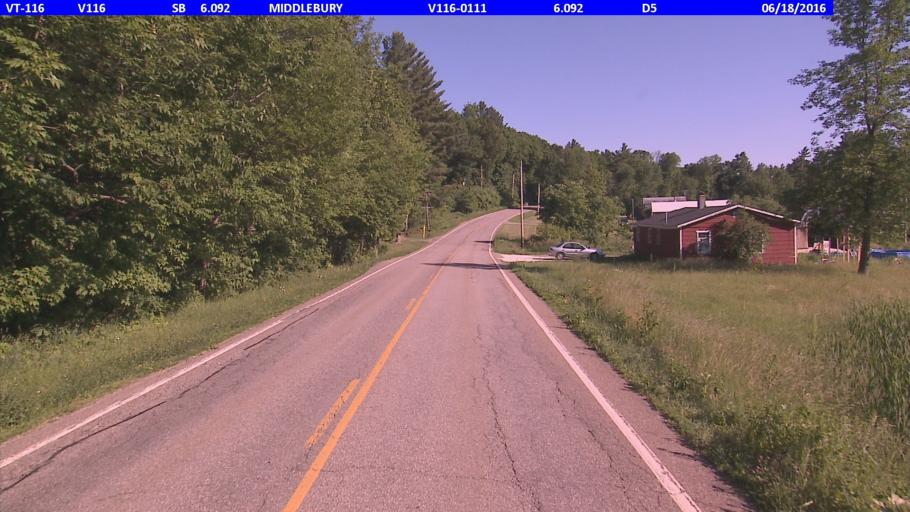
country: US
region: Vermont
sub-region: Addison County
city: Middlebury (village)
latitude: 44.0477
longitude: -73.0911
